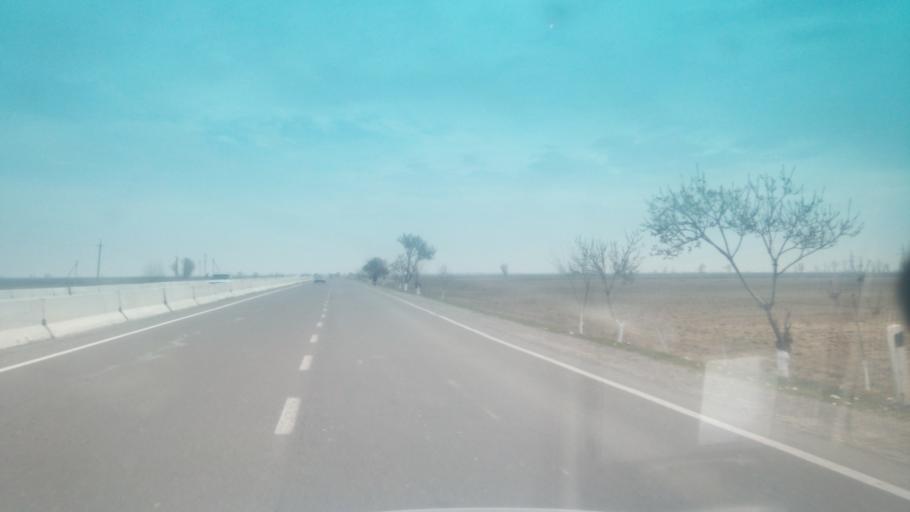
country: KZ
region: Ongtustik Qazaqstan
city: Myrzakent
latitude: 40.5207
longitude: 68.4645
